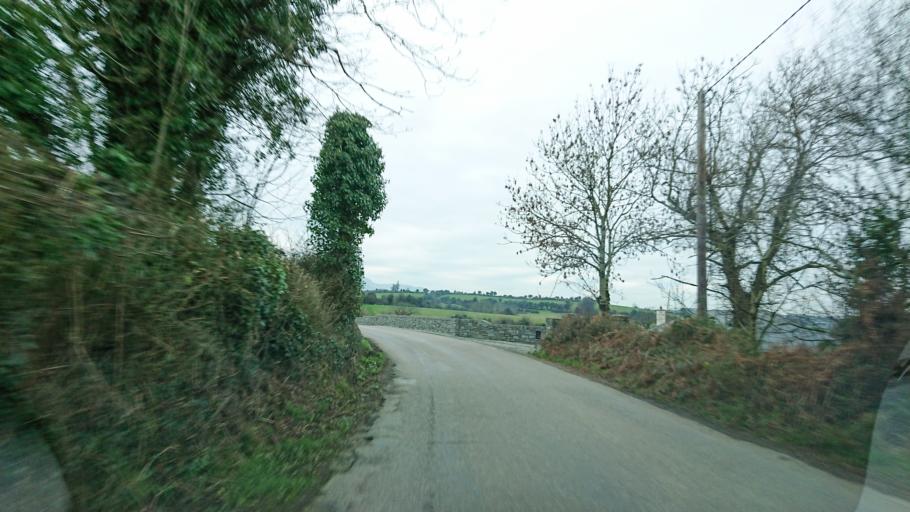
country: IE
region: Munster
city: Carrick-on-Suir
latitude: 52.2759
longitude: -7.4126
